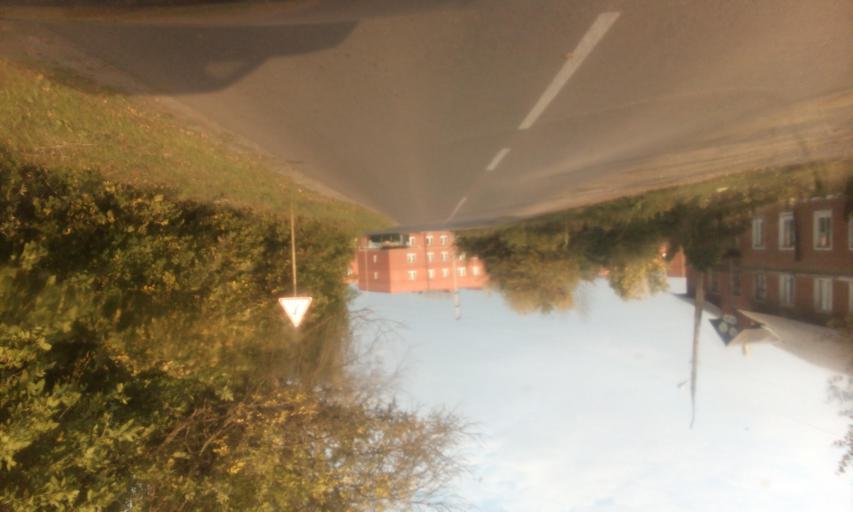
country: RU
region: Tula
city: Partizan
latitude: 53.9291
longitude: 38.1253
